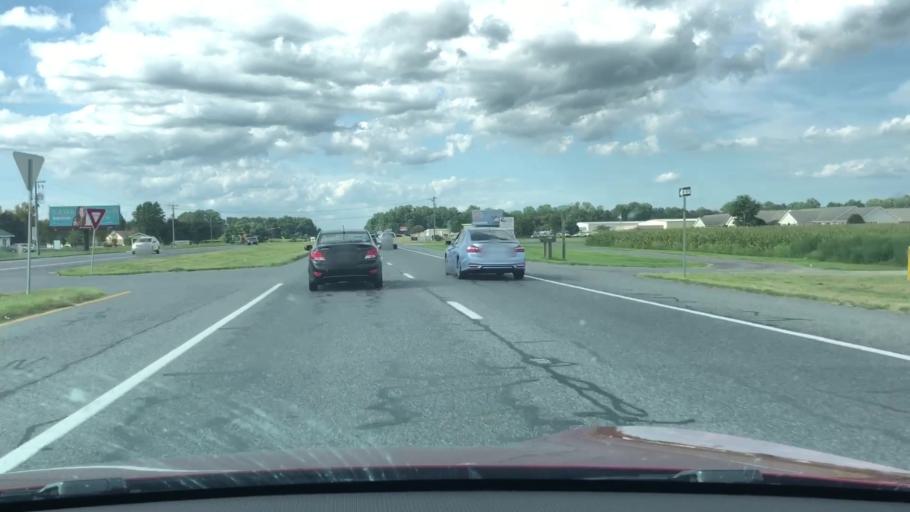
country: US
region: Delaware
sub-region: Sussex County
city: Bridgeville
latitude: 38.7371
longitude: -75.5918
